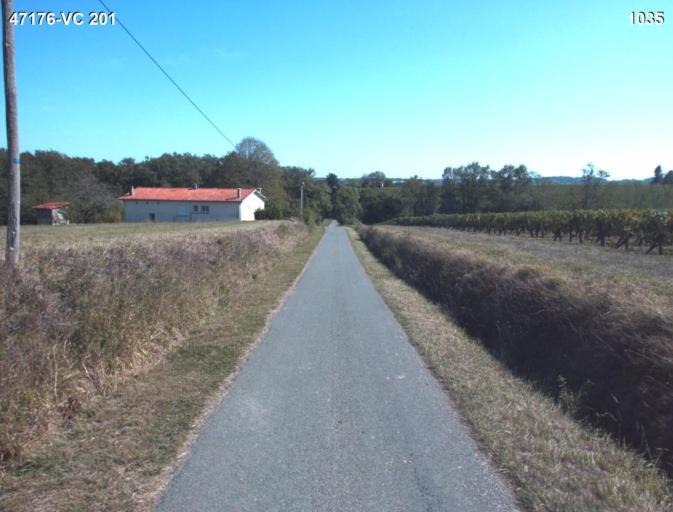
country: FR
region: Aquitaine
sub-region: Departement du Lot-et-Garonne
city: Vianne
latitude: 44.2134
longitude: 0.3021
